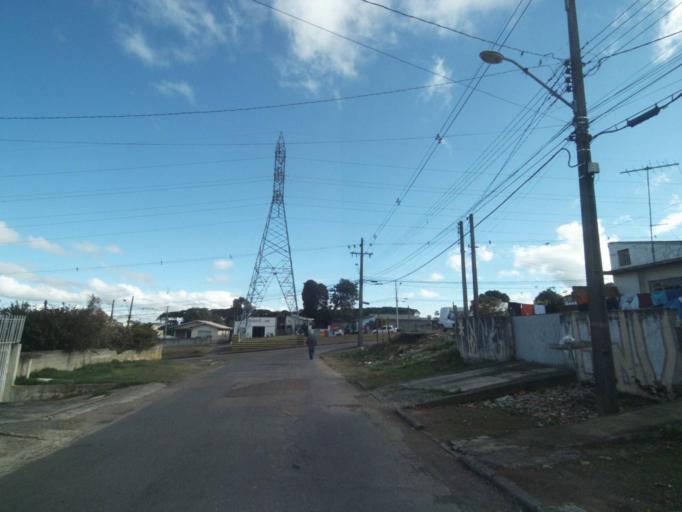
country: BR
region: Parana
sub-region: Sao Jose Dos Pinhais
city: Sao Jose dos Pinhais
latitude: -25.5331
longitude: -49.2839
